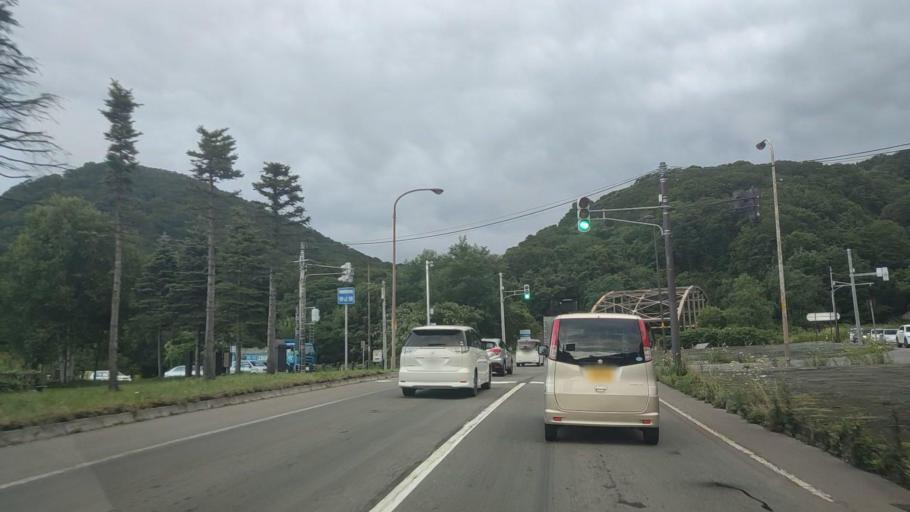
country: JP
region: Hokkaido
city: Nanae
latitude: 41.9568
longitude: 140.6504
